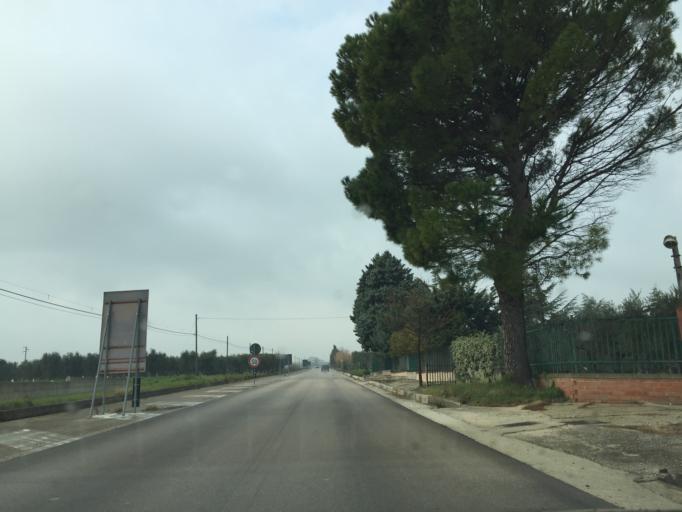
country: IT
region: Apulia
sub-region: Provincia di Foggia
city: Troia
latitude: 41.3773
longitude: 15.3622
